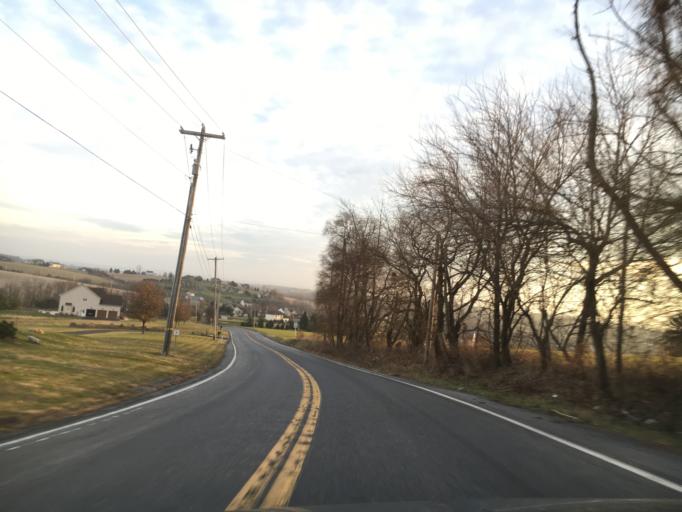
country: US
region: Pennsylvania
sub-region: Lehigh County
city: Slatington
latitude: 40.7095
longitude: -75.5972
